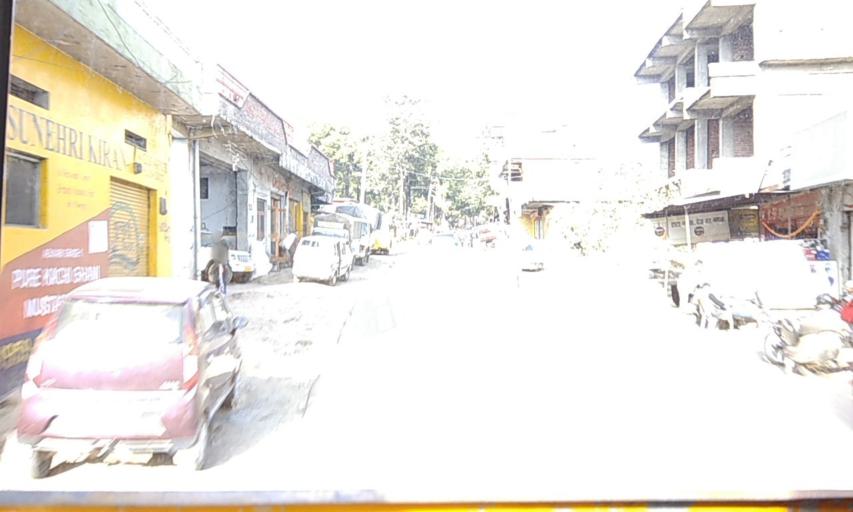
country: IN
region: Himachal Pradesh
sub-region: Kangra
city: Palampur
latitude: 32.0869
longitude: 76.5244
